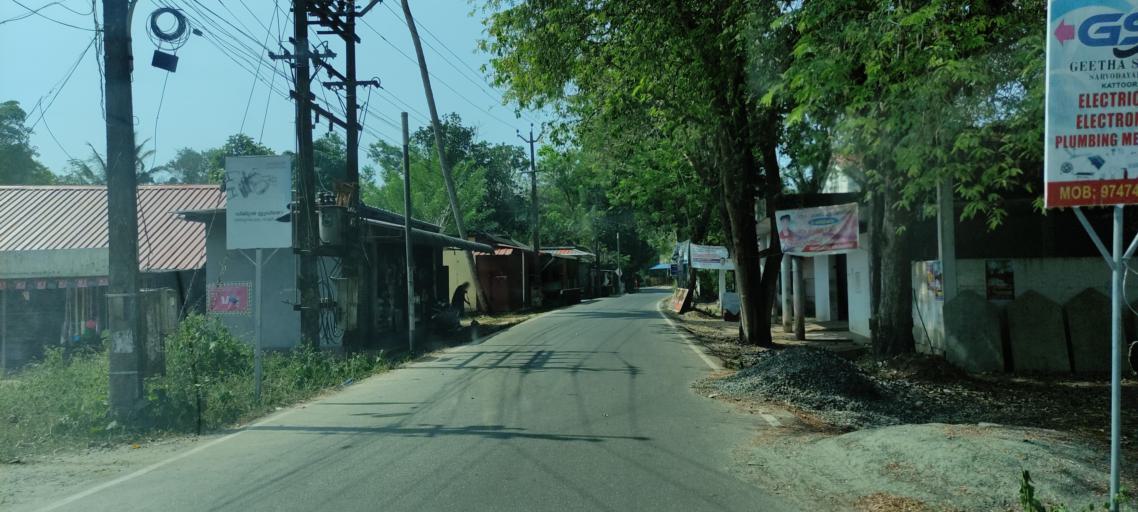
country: IN
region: Kerala
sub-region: Alappuzha
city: Alleppey
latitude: 9.5553
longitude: 76.3177
